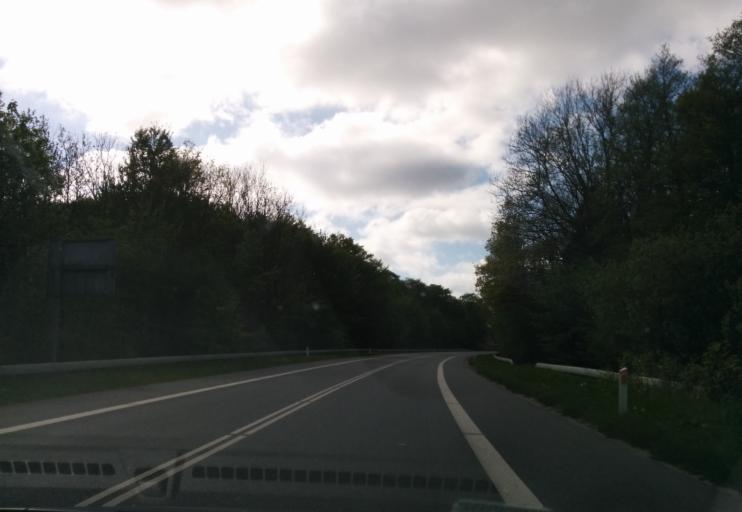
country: DK
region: South Denmark
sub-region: Assens Kommune
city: Vissenbjerg
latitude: 55.3925
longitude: 10.1133
